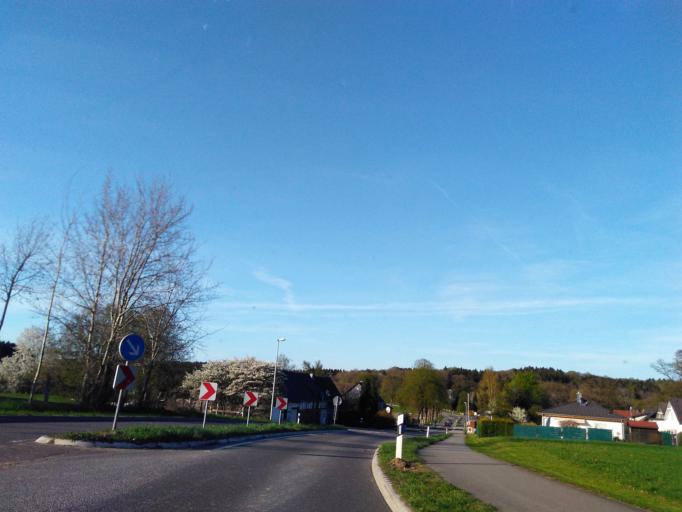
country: DE
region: North Rhine-Westphalia
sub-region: Regierungsbezirk Koln
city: Engelskirchen
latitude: 50.9541
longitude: 7.4561
